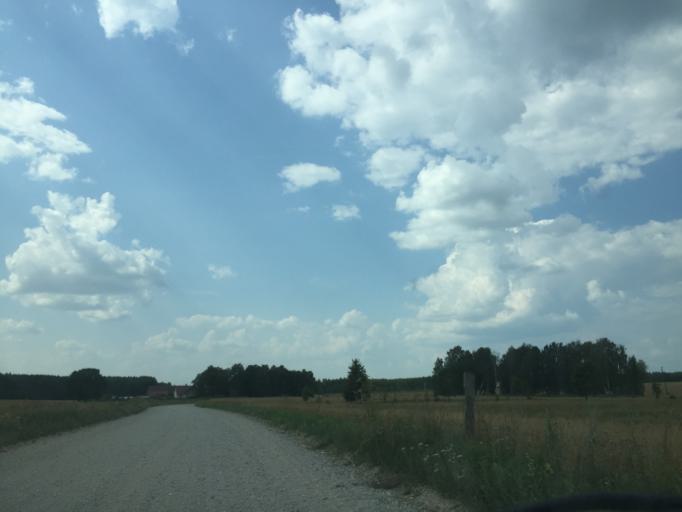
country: LV
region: Auces Novads
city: Auce
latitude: 56.4074
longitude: 23.0382
